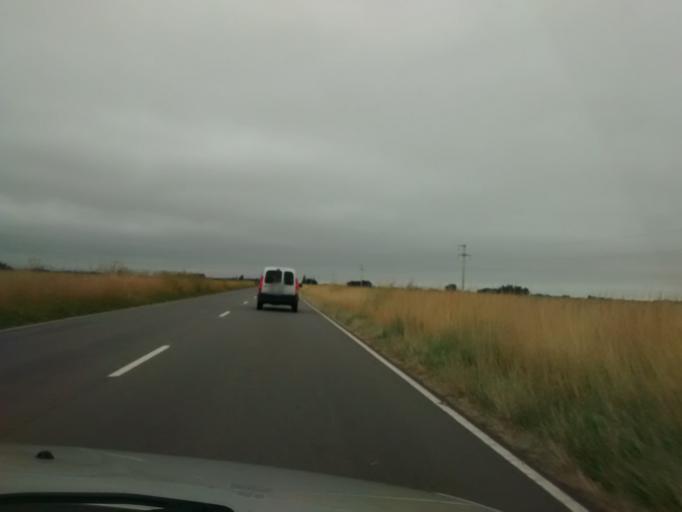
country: AR
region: Buenos Aires
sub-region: Partido de Ayacucho
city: Ayacucho
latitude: -37.0204
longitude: -58.5385
